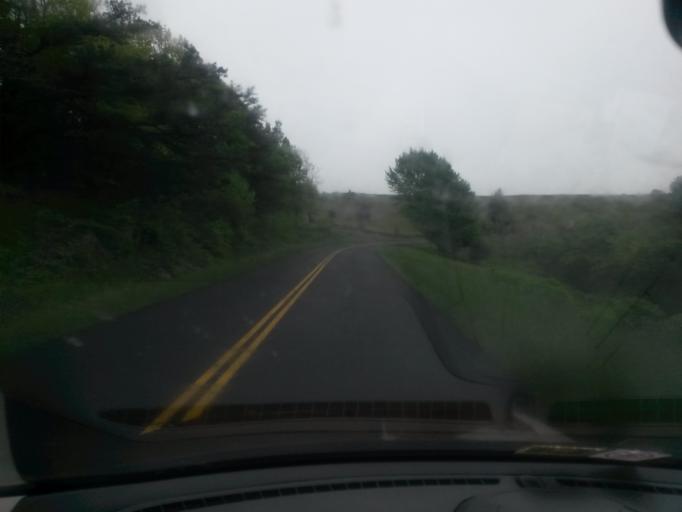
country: US
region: Virginia
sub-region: Floyd County
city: Floyd
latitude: 36.8059
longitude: -80.3616
